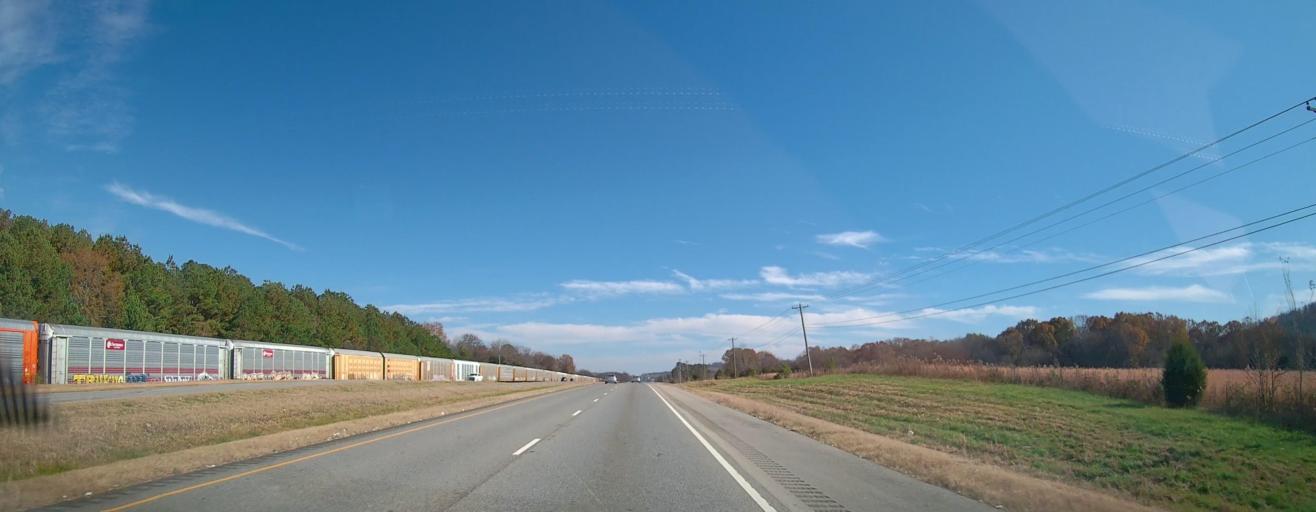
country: US
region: Alabama
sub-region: Colbert County
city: Tuscumbia
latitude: 34.7265
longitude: -87.8330
